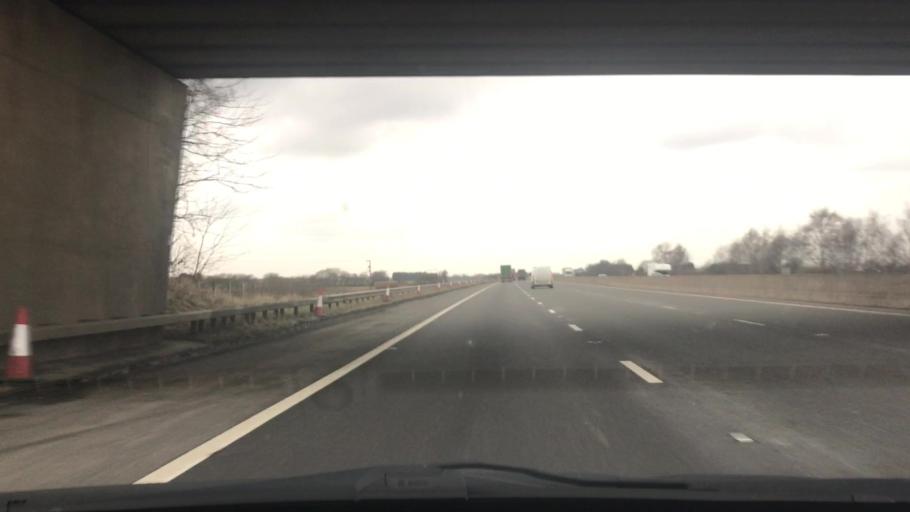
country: GB
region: England
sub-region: Doncaster
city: Hatfield
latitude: 53.5757
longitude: -0.9218
